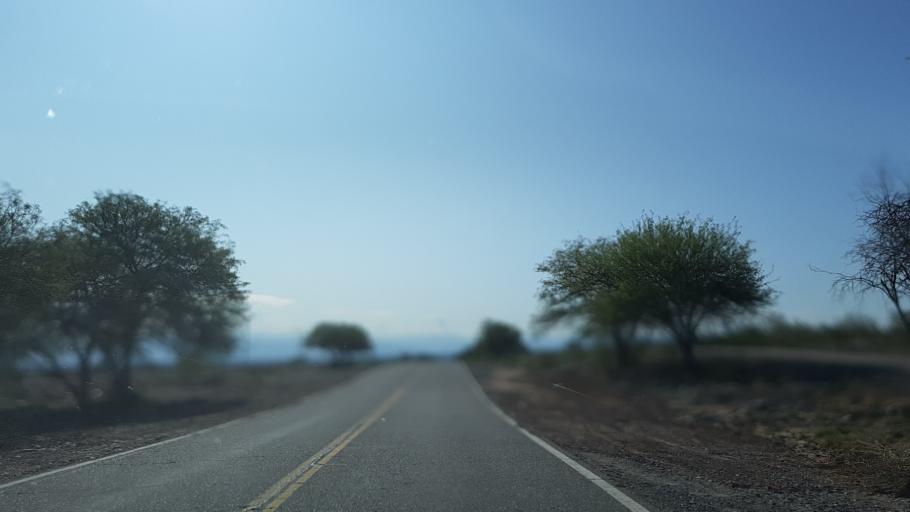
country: AR
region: San Juan
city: Caucete
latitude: -31.7544
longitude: -68.0832
